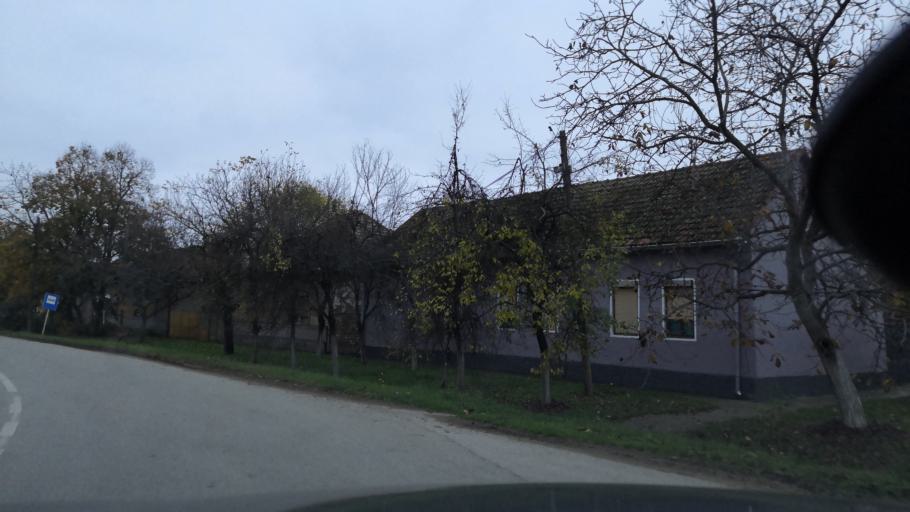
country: RS
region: Autonomna Pokrajina Vojvodina
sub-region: Severnobanatski Okrug
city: Kanjiza
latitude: 46.1260
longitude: 20.0925
